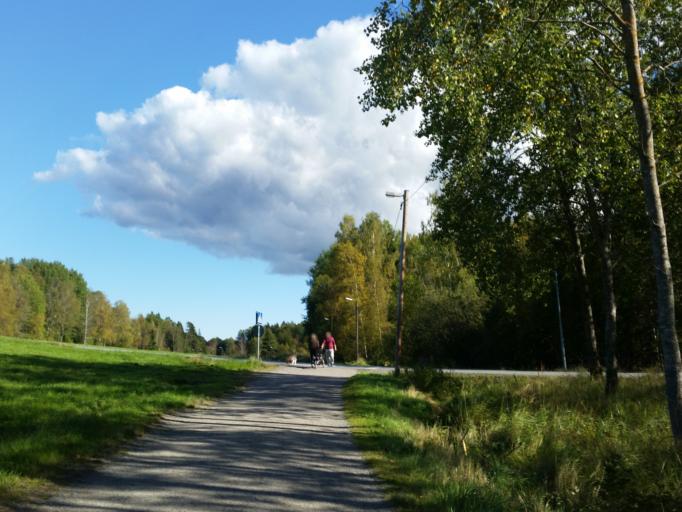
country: SE
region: Stockholm
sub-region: Haninge Kommun
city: Haninge
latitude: 59.1676
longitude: 18.2118
